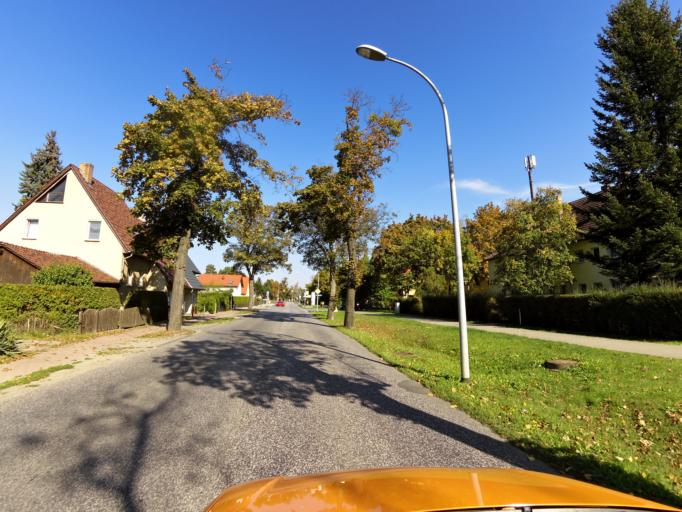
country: DE
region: Brandenburg
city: Stahnsdorf
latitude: 52.3781
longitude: 13.2075
